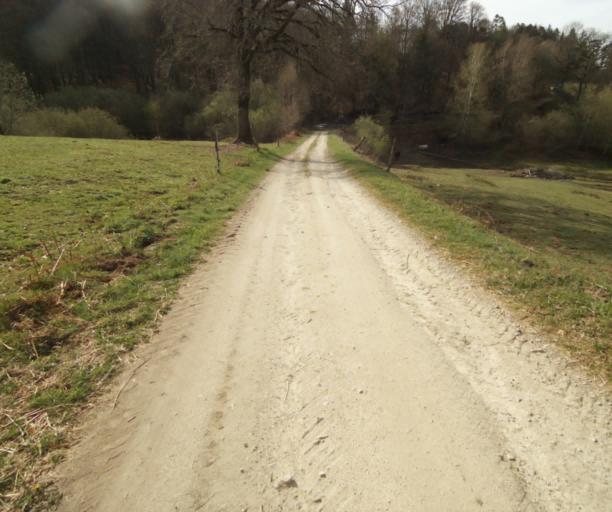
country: FR
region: Limousin
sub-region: Departement de la Correze
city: Correze
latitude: 45.3474
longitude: 1.8646
